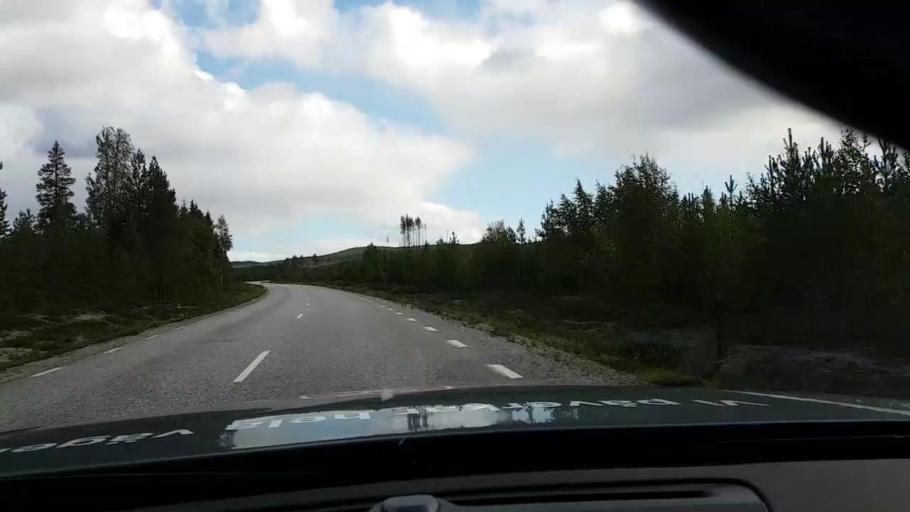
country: SE
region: Vaesternorrland
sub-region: OErnskoeldsviks Kommun
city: Bredbyn
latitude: 63.6807
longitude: 17.7847
